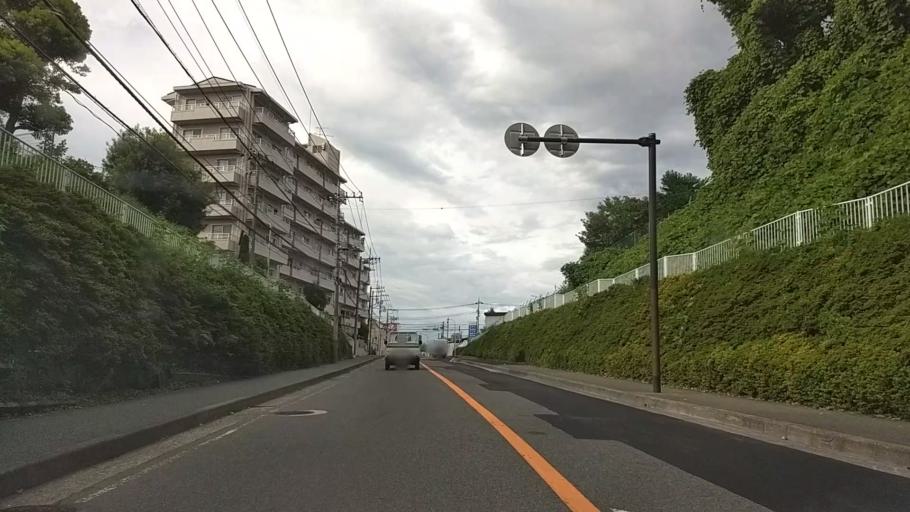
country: JP
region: Tokyo
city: Hachioji
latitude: 35.5766
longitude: 139.3412
